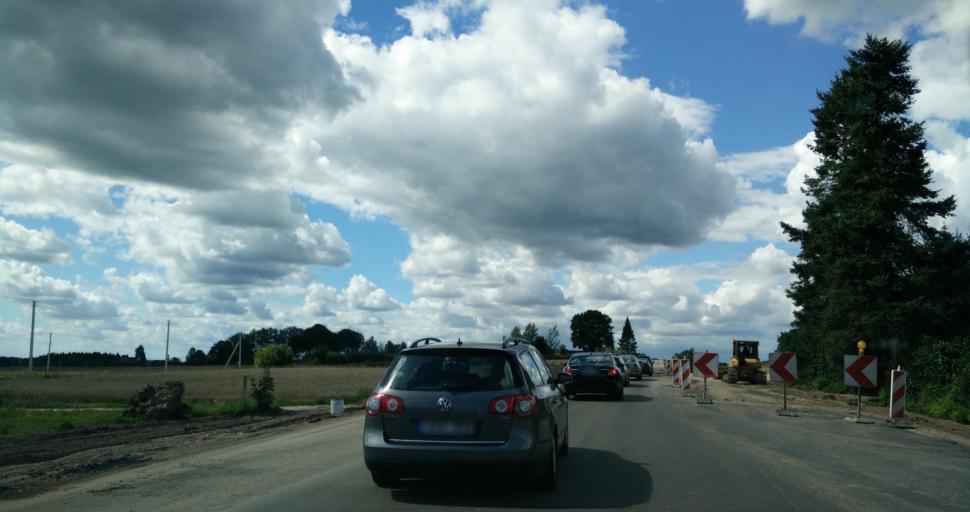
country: LT
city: Kulautuva
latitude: 54.9566
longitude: 23.6596
